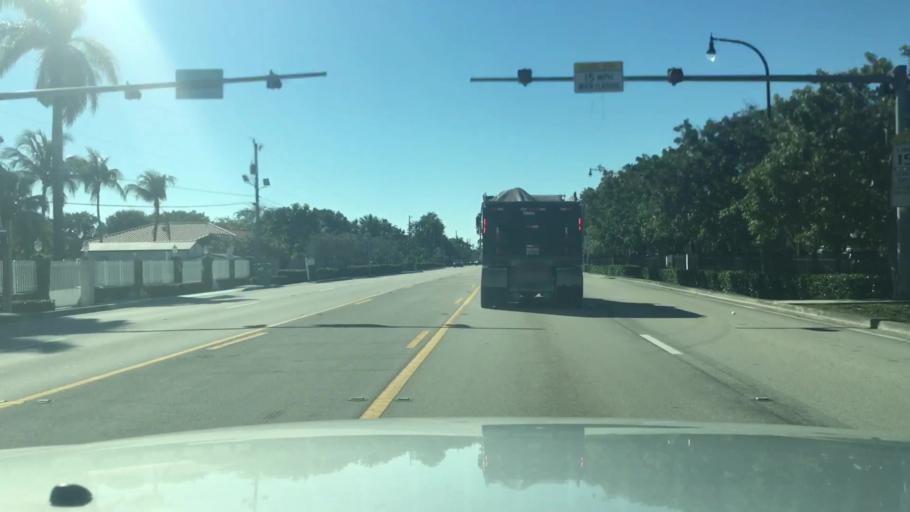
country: US
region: Florida
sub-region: Miami-Dade County
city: Tamiami
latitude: 25.7670
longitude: -80.4010
